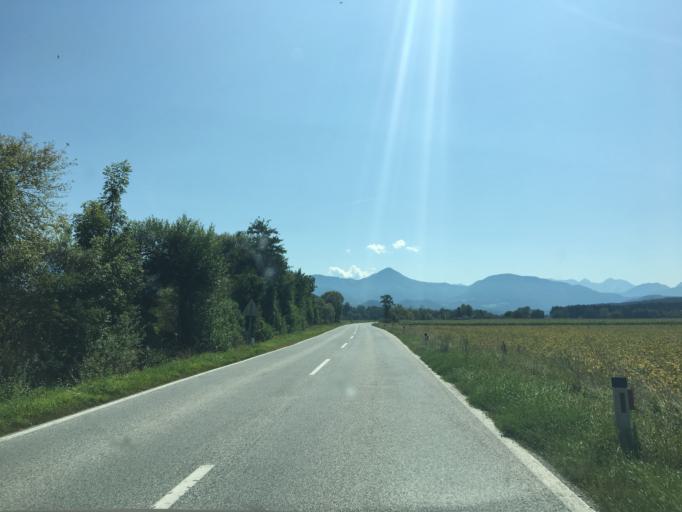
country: AT
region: Carinthia
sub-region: Politischer Bezirk Volkermarkt
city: Eberndorf
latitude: 46.6156
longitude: 14.6355
